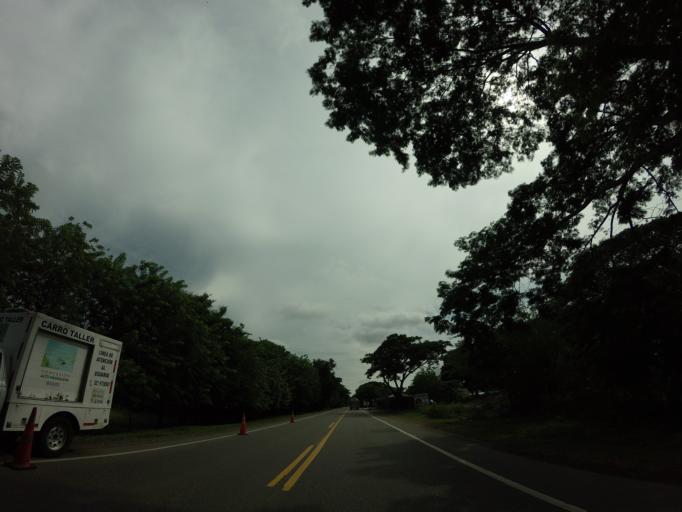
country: CO
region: Caldas
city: La Dorada
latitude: 5.4315
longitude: -74.6808
